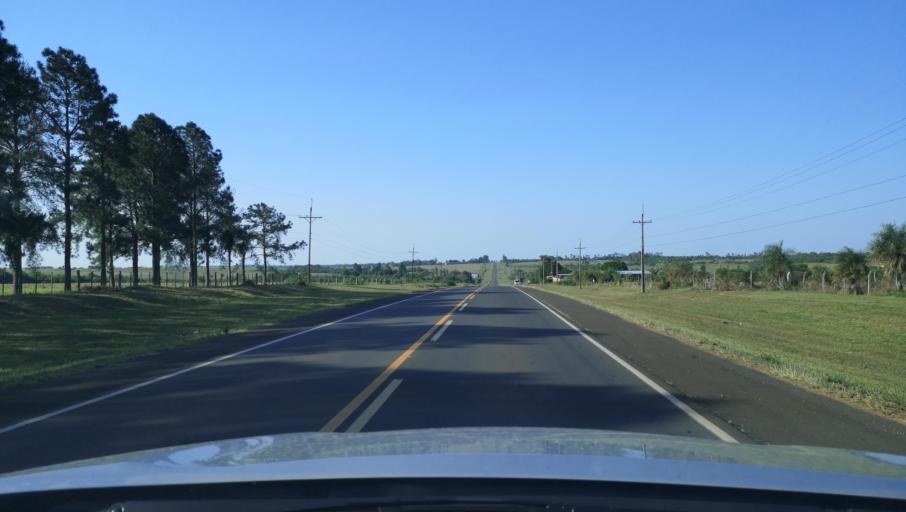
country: PY
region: Misiones
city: Santa Maria
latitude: -26.8397
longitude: -57.0356
